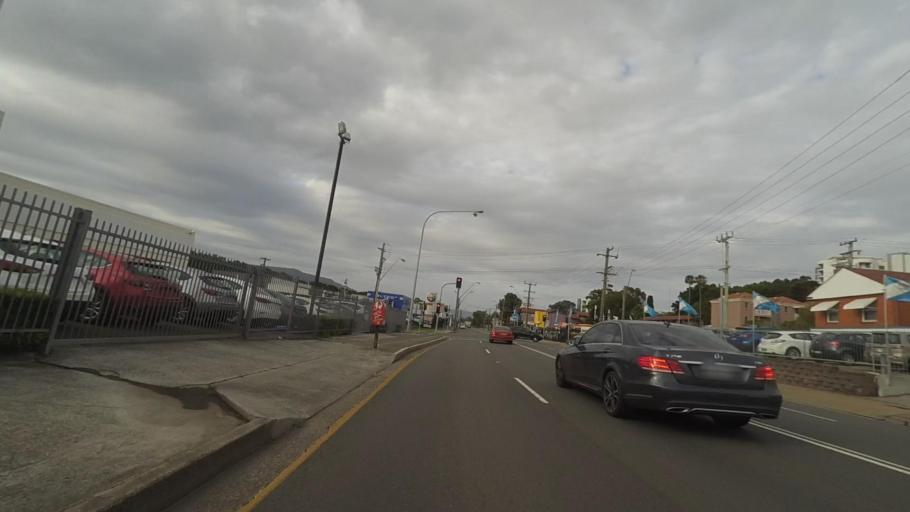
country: AU
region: New South Wales
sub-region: Wollongong
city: Gwynneville
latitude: -34.4178
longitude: 150.8923
